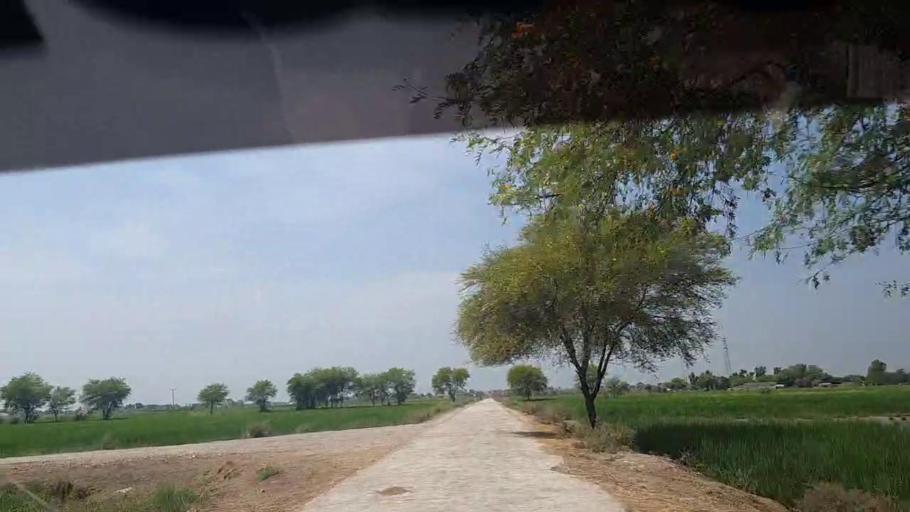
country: PK
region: Sindh
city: Thul
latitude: 28.1757
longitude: 68.7379
